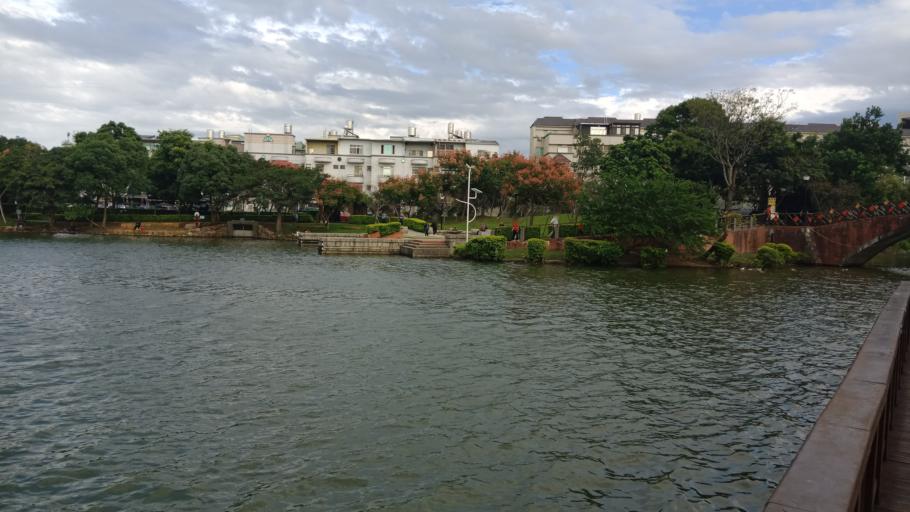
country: TW
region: Taiwan
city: Daxi
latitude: 24.8599
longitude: 121.2098
